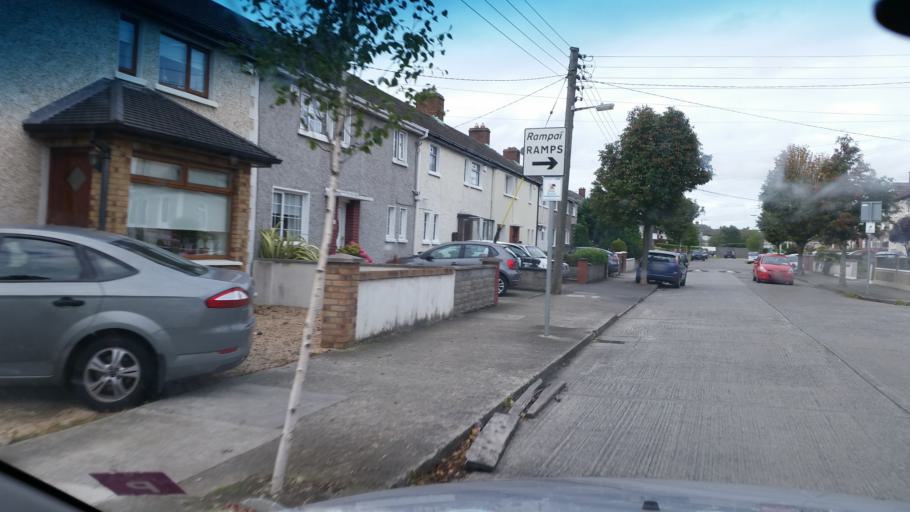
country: IE
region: Leinster
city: Glasnevin
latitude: 53.3872
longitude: -6.2723
